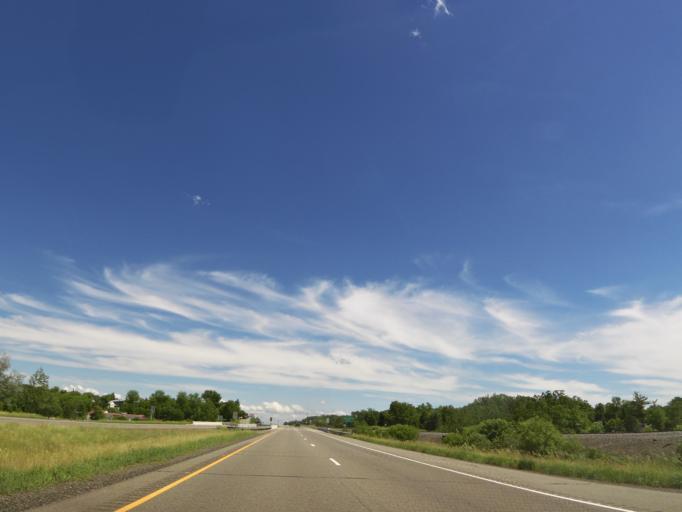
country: US
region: Minnesota
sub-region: Todd County
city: Staples
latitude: 46.3753
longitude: -94.9433
